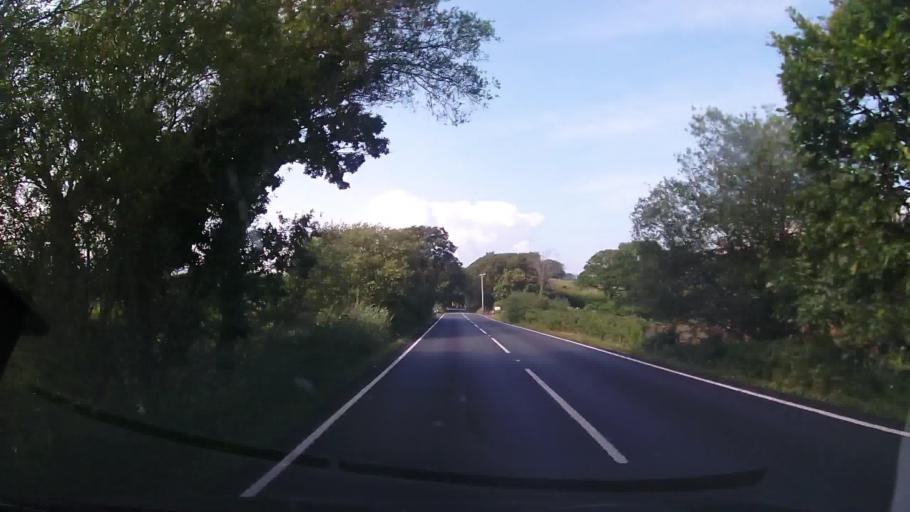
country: GB
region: Wales
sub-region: Gwynedd
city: Penrhyndeudraeth
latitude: 52.9127
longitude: -4.0526
